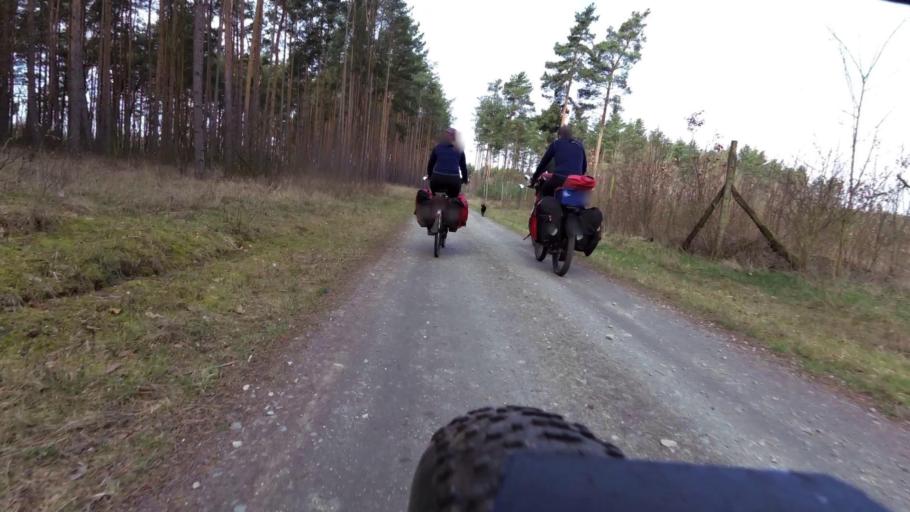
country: DE
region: Brandenburg
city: Ziltendorf
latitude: 52.2809
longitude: 14.6578
